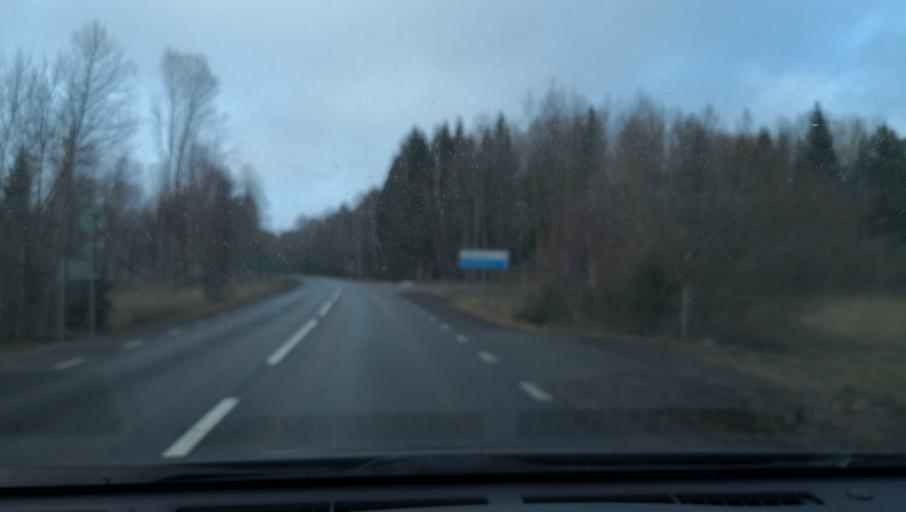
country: SE
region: Vaestra Goetaland
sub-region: Gullspangs Kommun
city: Gullspang
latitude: 58.9543
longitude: 14.0771
